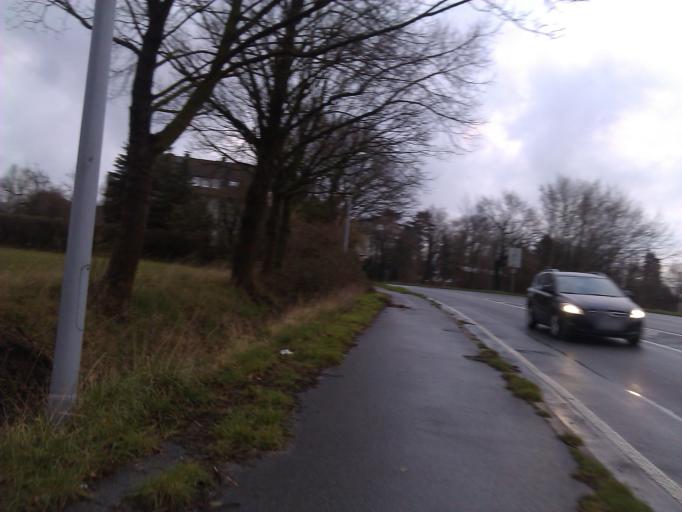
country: DE
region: North Rhine-Westphalia
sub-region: Regierungsbezirk Dusseldorf
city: Heiligenhaus
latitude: 51.3857
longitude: 6.9427
